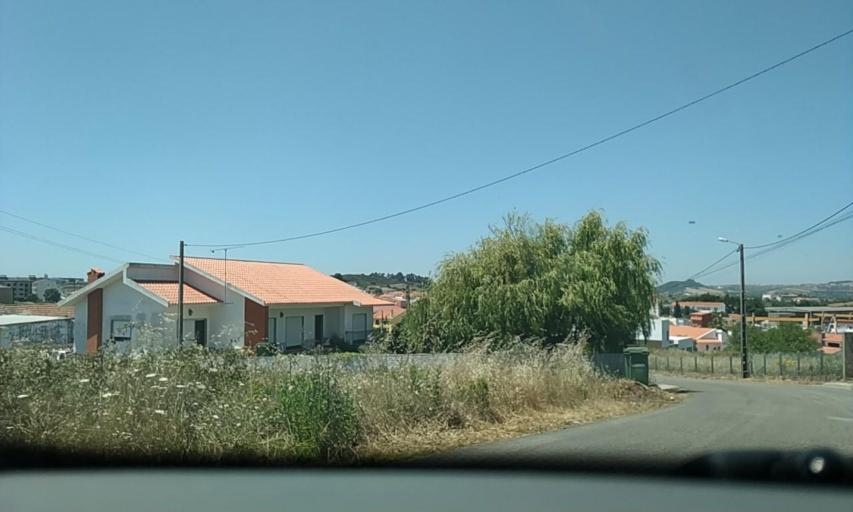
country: PT
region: Lisbon
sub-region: Sintra
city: Pero Pinheiro
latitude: 38.8643
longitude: -9.3118
